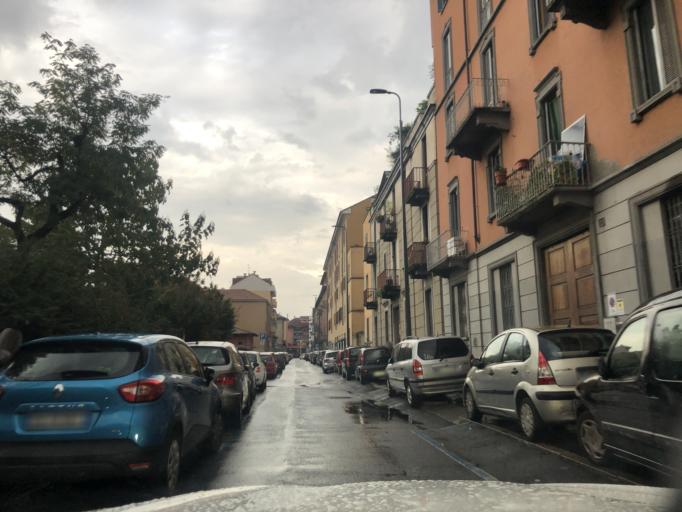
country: IT
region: Lombardy
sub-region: Citta metropolitana di Milano
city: Bresso
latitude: 45.5032
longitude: 9.1774
